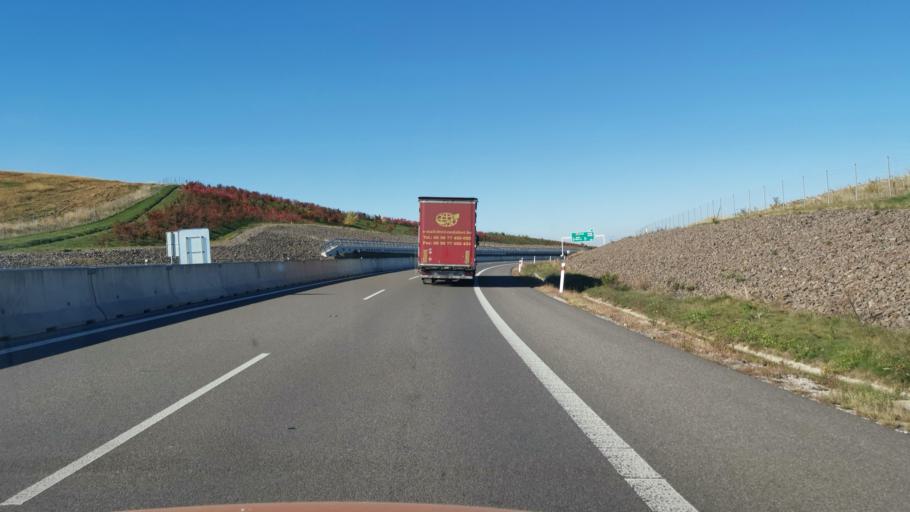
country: HU
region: Borsod-Abauj-Zemplen
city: Gonc
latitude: 48.5414
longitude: 21.2386
